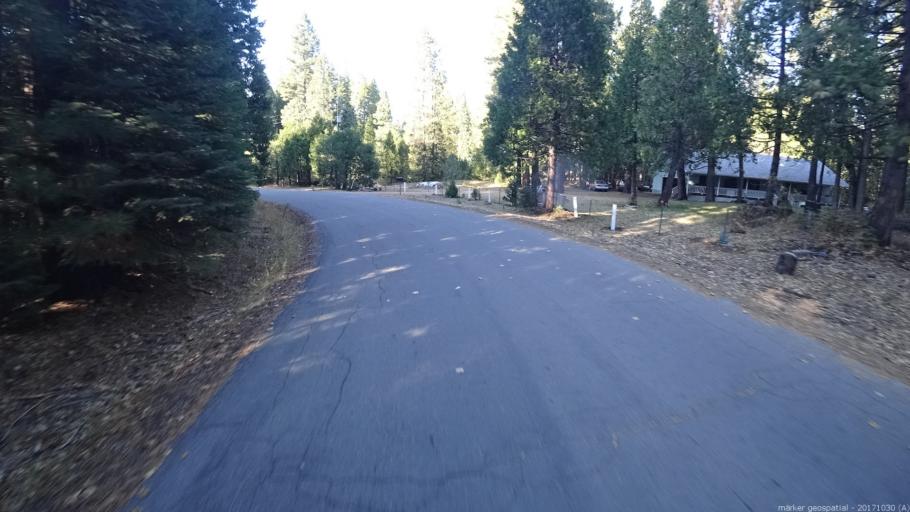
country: US
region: California
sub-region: Shasta County
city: Shingletown
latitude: 40.5578
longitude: -121.7171
